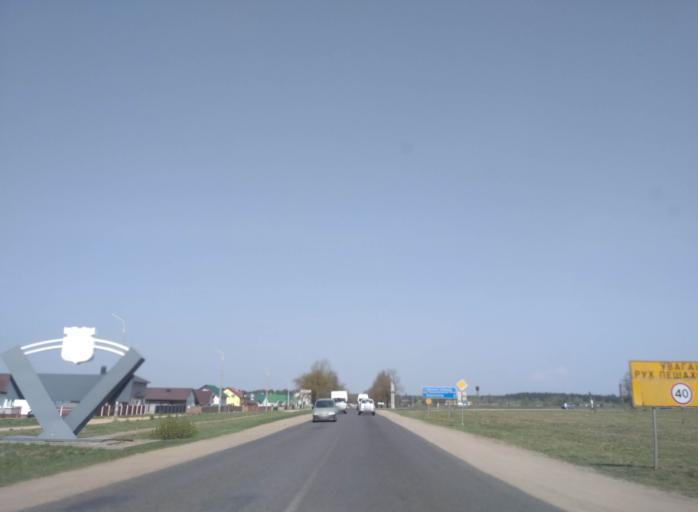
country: BY
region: Minsk
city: Horad Barysaw
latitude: 54.2728
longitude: 28.4971
